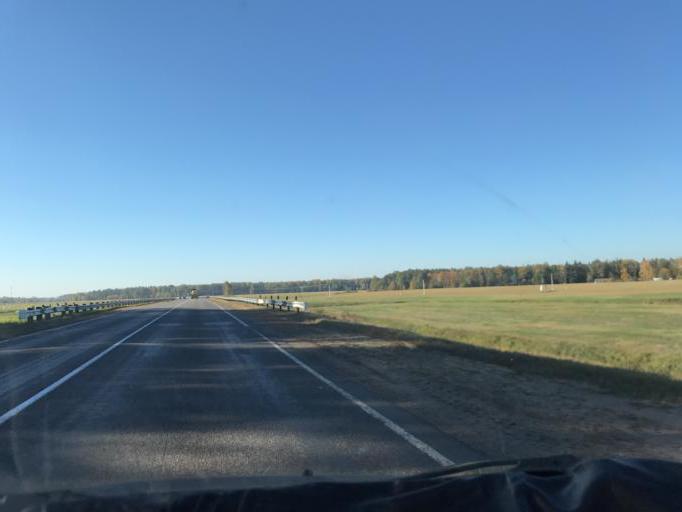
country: BY
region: Mogilev
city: Babruysk
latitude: 53.1992
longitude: 29.0628
